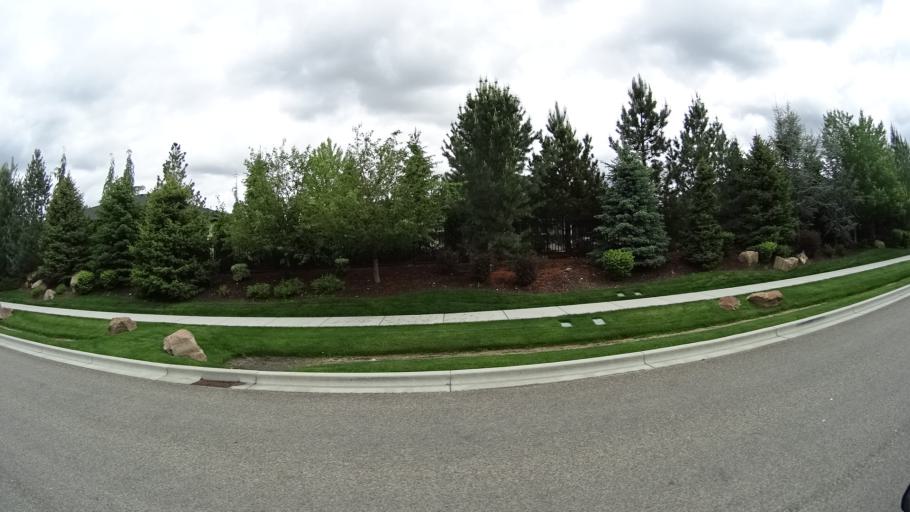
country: US
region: Idaho
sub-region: Ada County
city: Eagle
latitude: 43.6860
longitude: -116.3617
